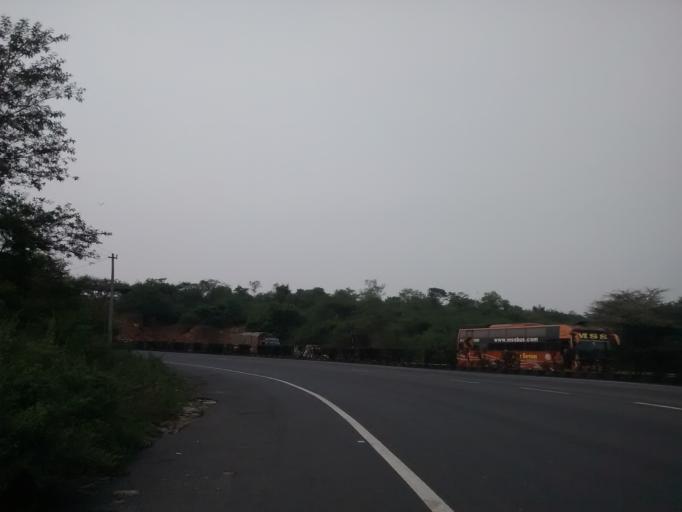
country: IN
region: Tamil Nadu
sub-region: Dharmapuri
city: Dharmapuri
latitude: 11.9636
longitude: 78.0513
